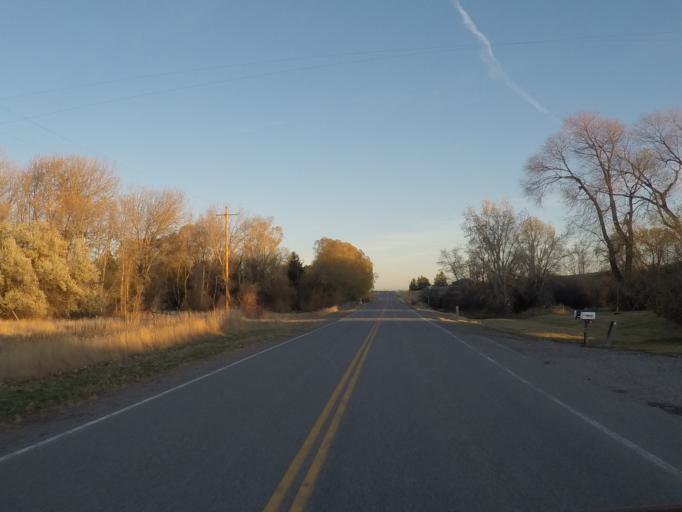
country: US
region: Montana
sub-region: Sweet Grass County
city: Big Timber
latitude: 45.7742
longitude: -109.8025
